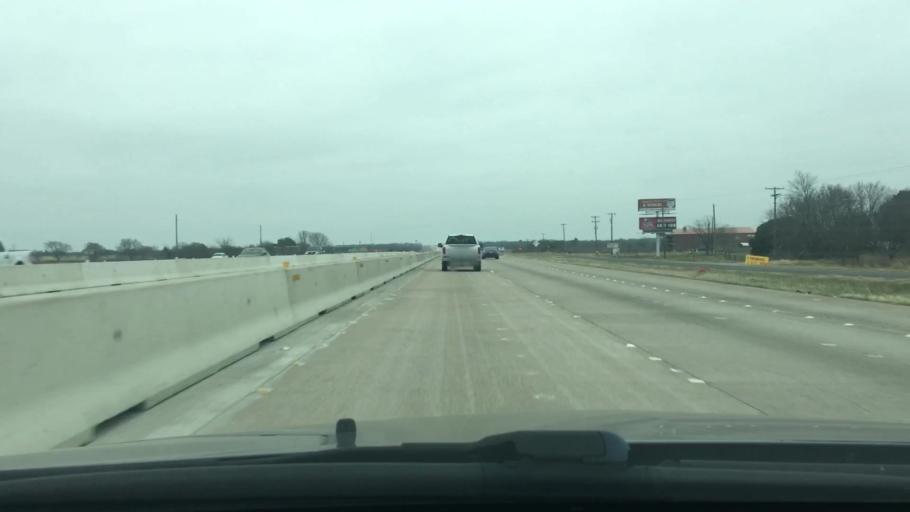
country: US
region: Texas
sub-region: Navarro County
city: Corsicana
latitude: 32.0332
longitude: -96.4439
